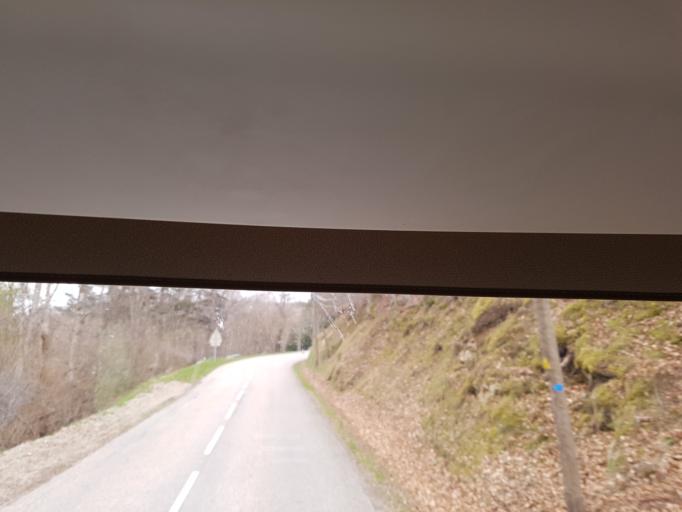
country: FR
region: Languedoc-Roussillon
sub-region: Departement de l'Aude
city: Quillan
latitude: 42.7017
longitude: 2.0915
